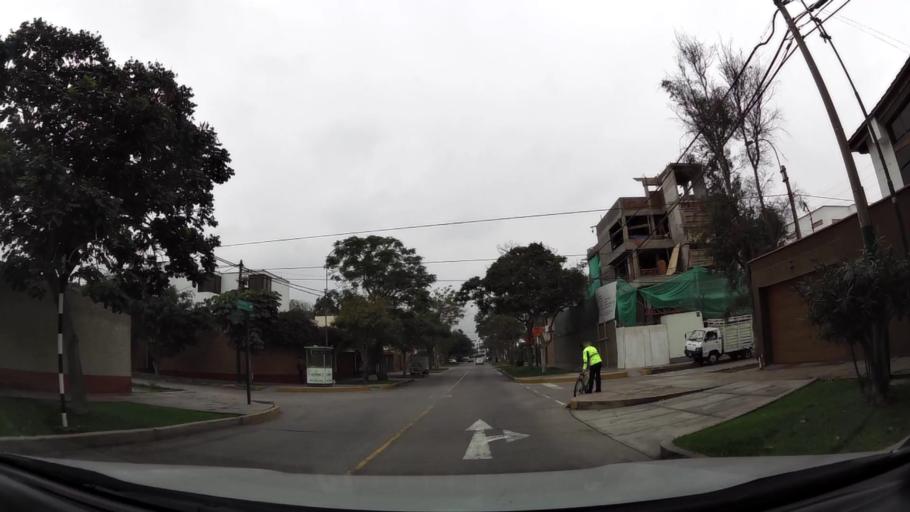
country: PE
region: Lima
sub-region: Lima
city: Surco
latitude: -12.1307
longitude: -77.0071
